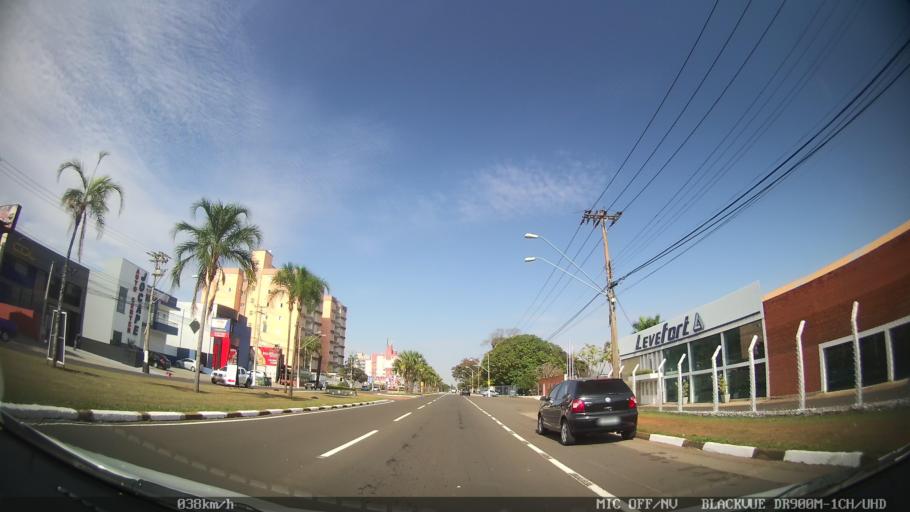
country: BR
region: Sao Paulo
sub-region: Paulinia
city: Paulinia
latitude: -22.7802
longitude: -47.1432
